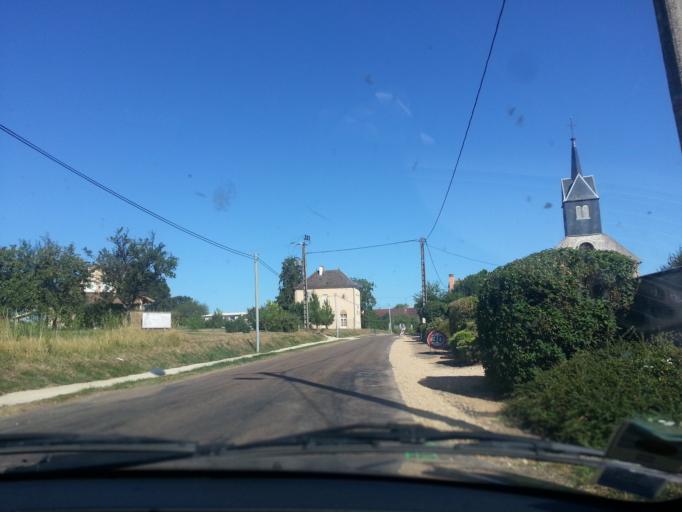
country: FR
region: Bourgogne
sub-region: Departement de Saone-et-Loire
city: Saint-Martin-en-Bresse
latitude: 46.7872
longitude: 5.0290
